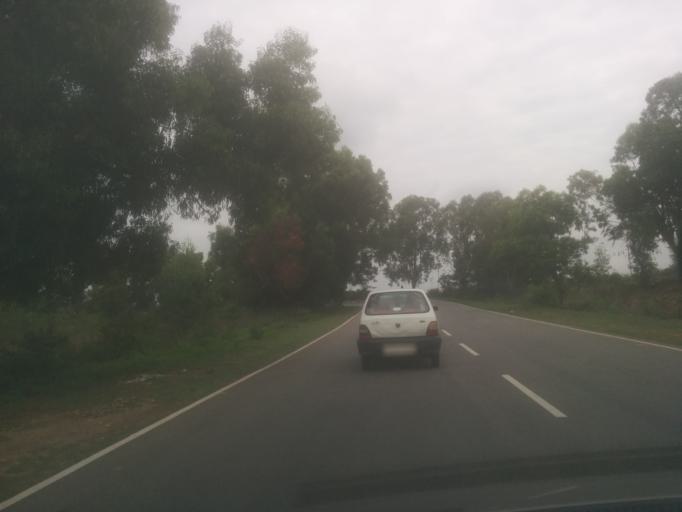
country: IN
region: Karnataka
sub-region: Hassan
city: Belur
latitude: 13.1618
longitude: 75.9003
